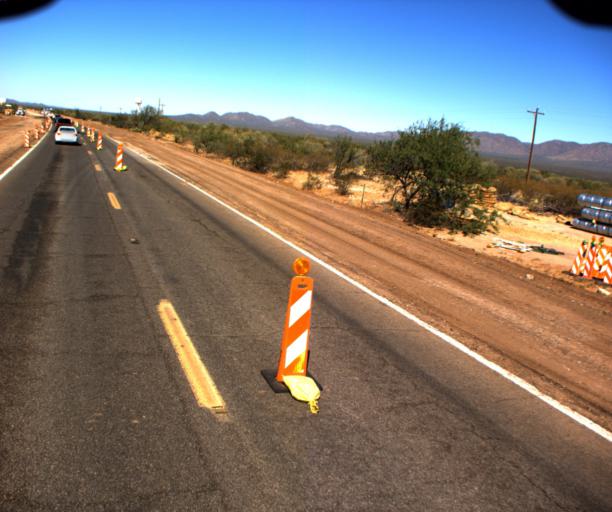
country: US
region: Arizona
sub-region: Pima County
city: Sells
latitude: 31.9949
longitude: -111.7017
